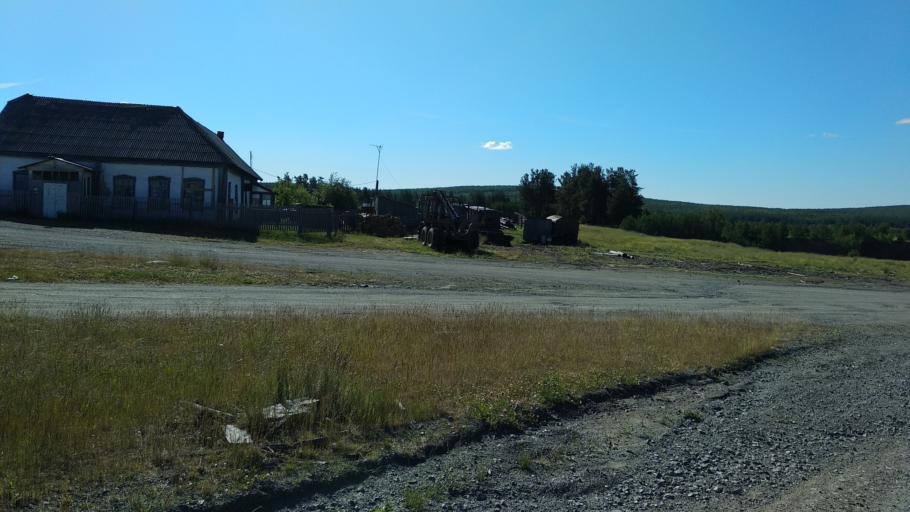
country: RU
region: Sverdlovsk
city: Severoural'sk
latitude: 60.1580
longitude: 59.7400
